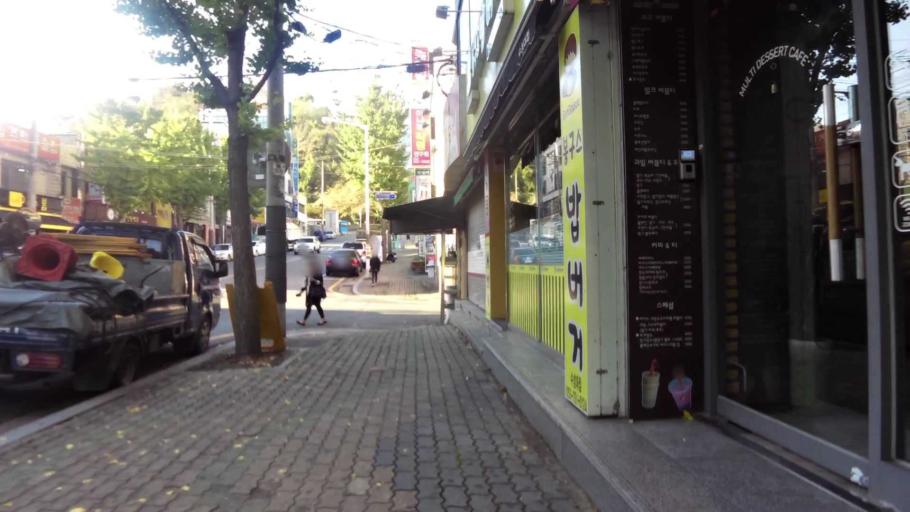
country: KR
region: Daegu
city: Daegu
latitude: 35.8561
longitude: 128.6501
